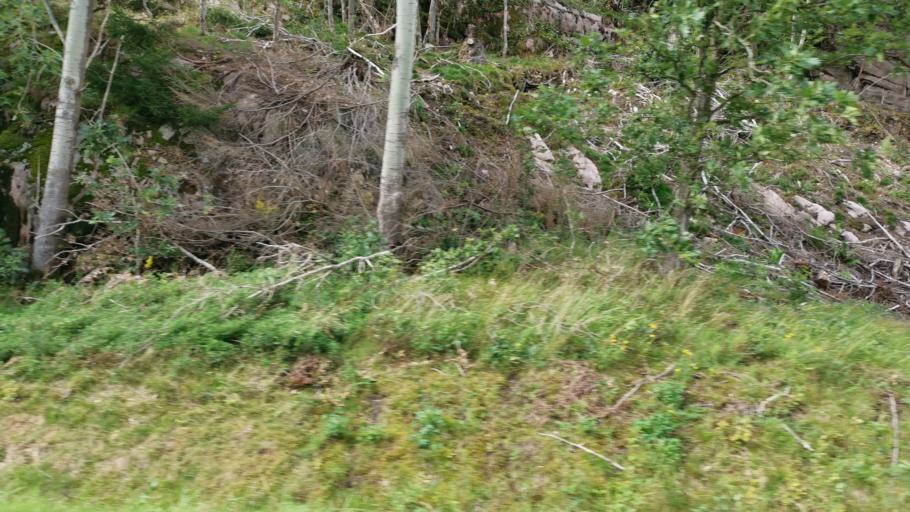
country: SE
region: Vaestra Goetaland
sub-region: Lysekils Kommun
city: Brastad
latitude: 58.4640
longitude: 11.4579
